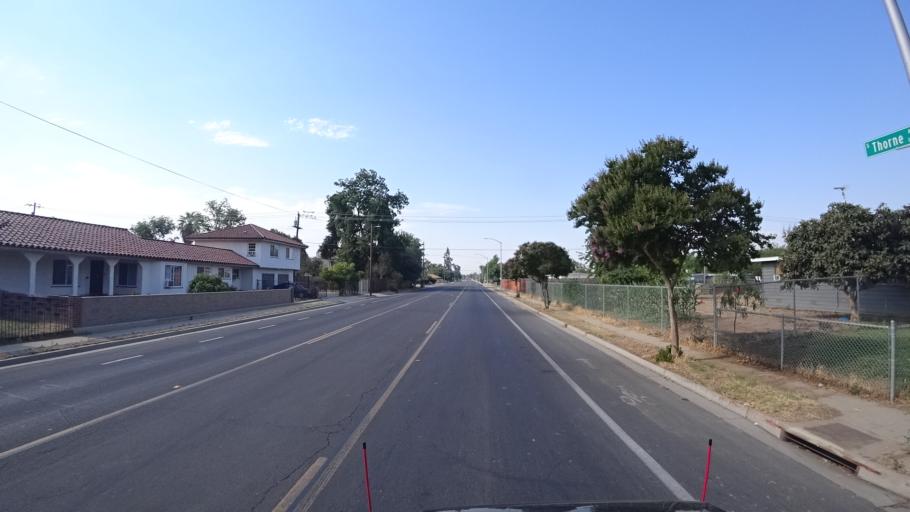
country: US
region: California
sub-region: Fresno County
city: West Park
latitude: 36.7263
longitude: -119.8132
